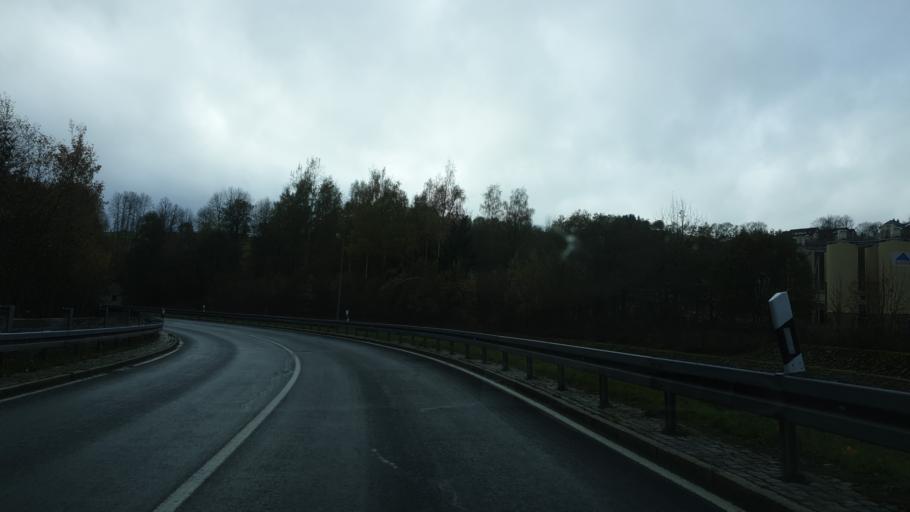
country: DE
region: Saxony
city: Schoenheide
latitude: 50.5036
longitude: 12.5545
